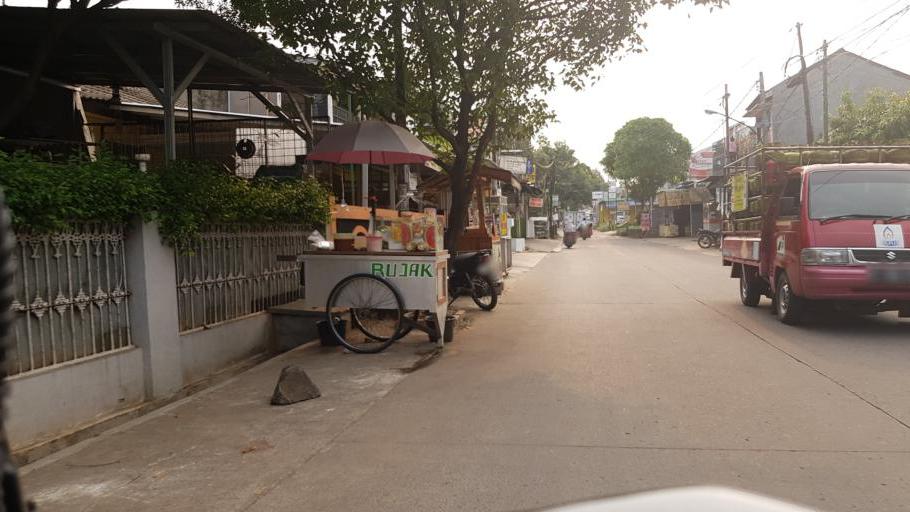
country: ID
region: West Java
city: Depok
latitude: -6.3724
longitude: 106.8490
